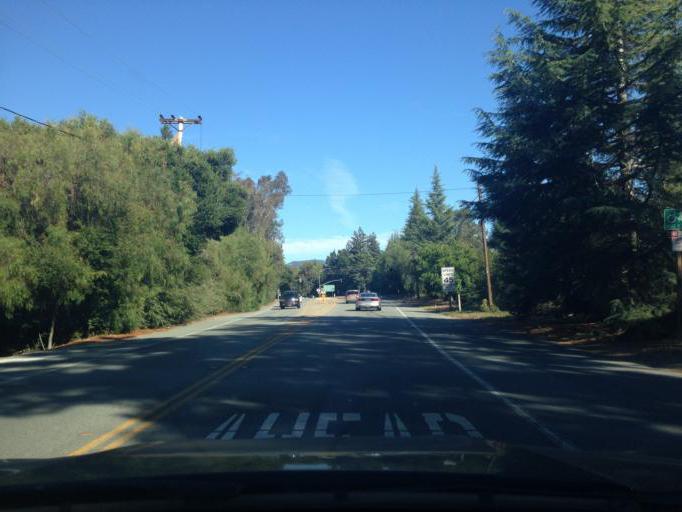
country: US
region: California
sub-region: Santa Clara County
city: Saratoga
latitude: 37.2472
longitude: -122.0159
